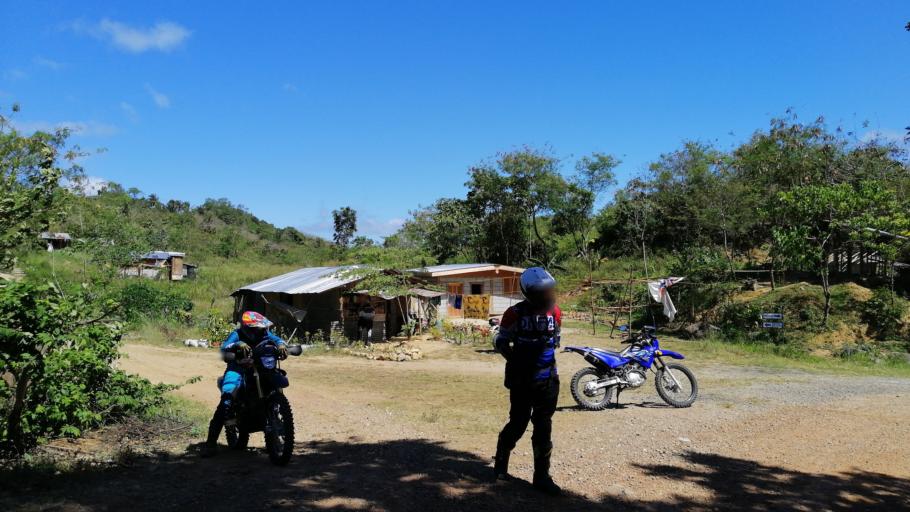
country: PH
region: Central Luzon
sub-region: Province of Bulacan
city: Akle
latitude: 15.0678
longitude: 121.1163
